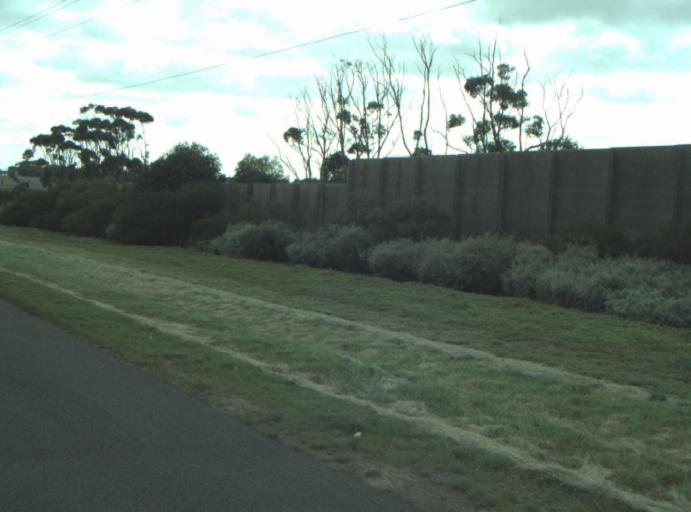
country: AU
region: Victoria
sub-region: Greater Geelong
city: Lara
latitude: -38.0421
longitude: 144.4084
